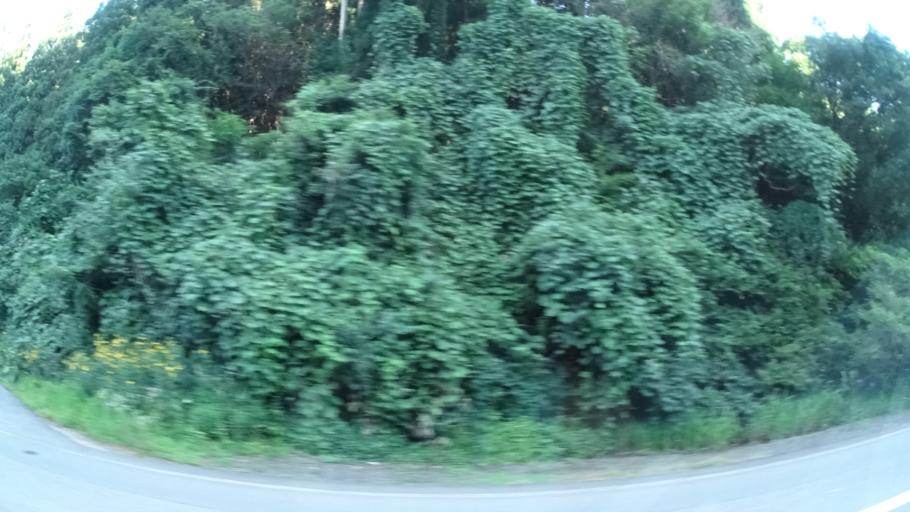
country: JP
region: Ishikawa
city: Nanao
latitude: 37.2918
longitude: 136.8924
